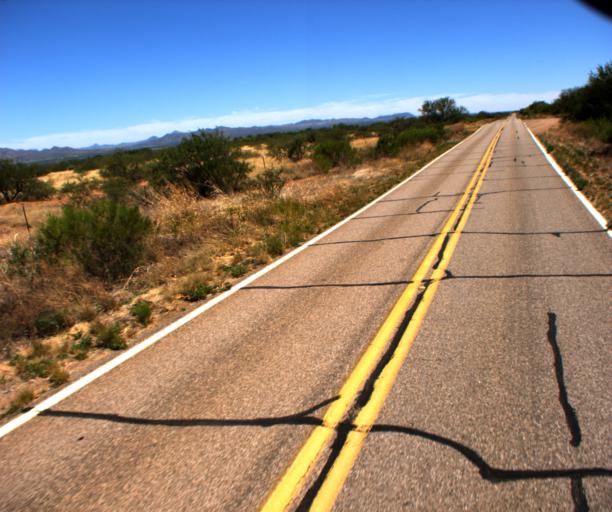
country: US
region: Arizona
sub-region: Pima County
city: Three Points
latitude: 31.7257
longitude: -111.4880
